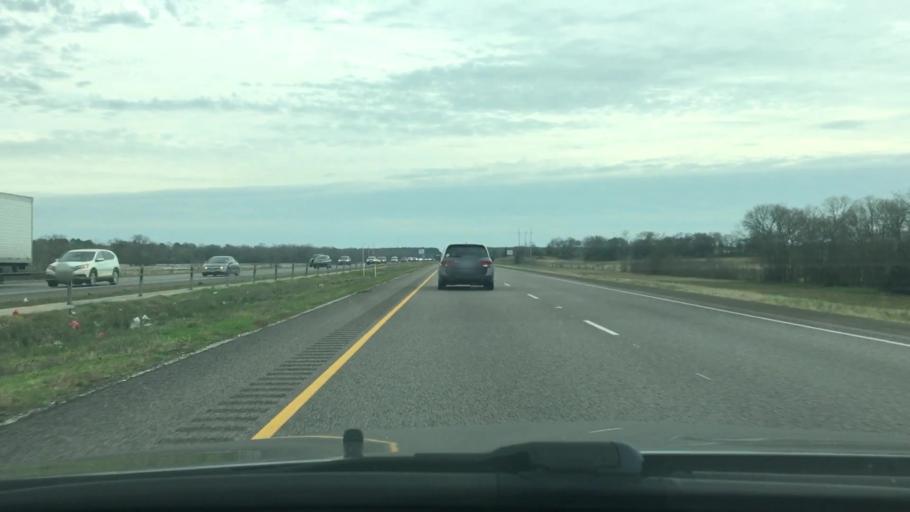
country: US
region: Texas
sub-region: Madison County
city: Madisonville
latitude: 30.9050
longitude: -95.7859
